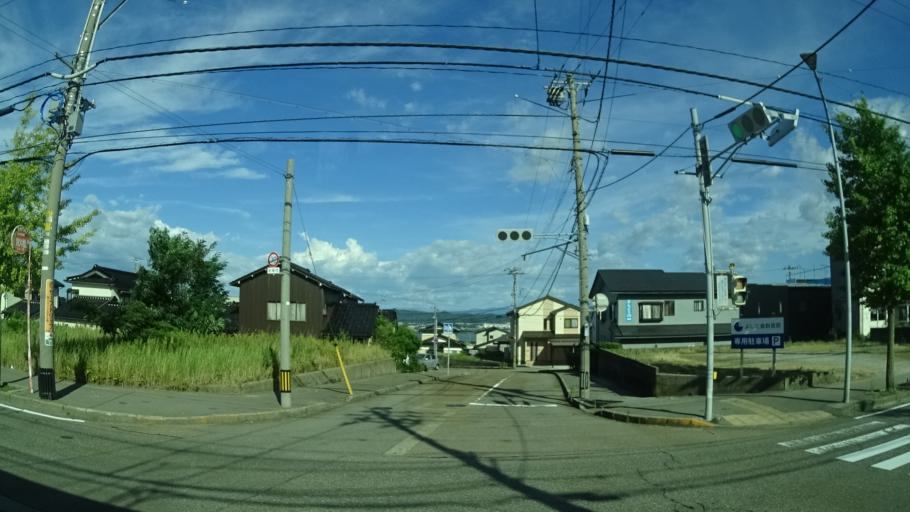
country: JP
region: Ishikawa
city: Kanazawa-shi
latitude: 36.6491
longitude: 136.6436
